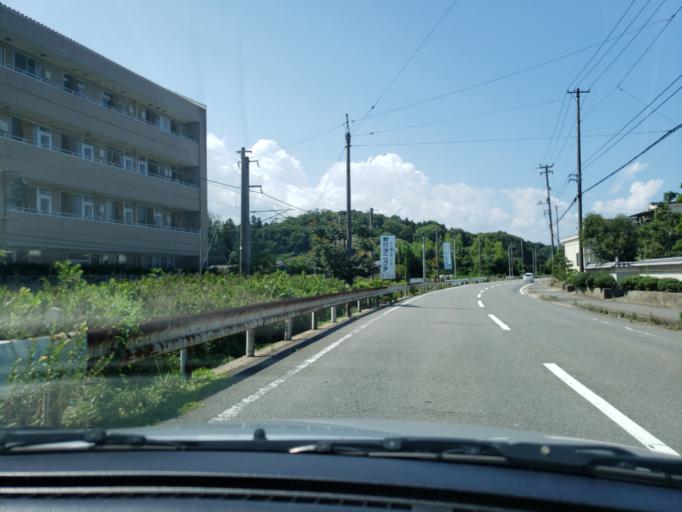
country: JP
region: Ehime
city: Hojo
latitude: 34.0890
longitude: 132.9318
